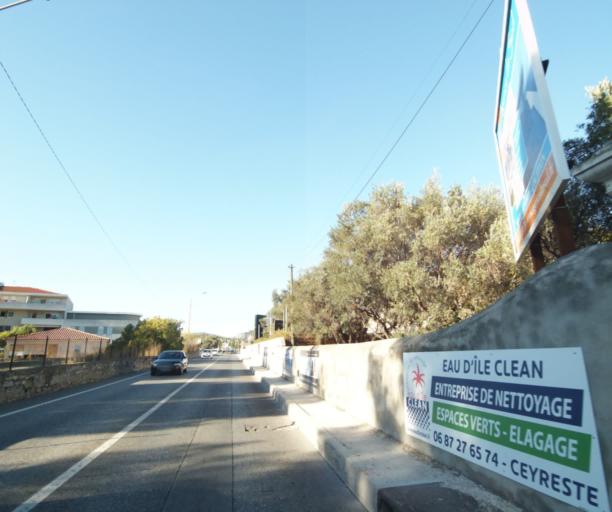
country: FR
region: Provence-Alpes-Cote d'Azur
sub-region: Departement des Bouches-du-Rhone
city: La Ciotat
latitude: 43.1865
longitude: 5.6070
